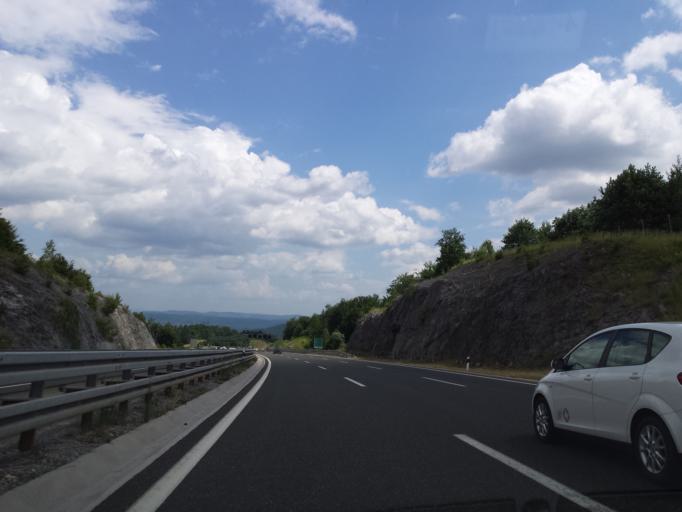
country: HR
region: Primorsko-Goranska
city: Vrbovsko
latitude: 45.3882
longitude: 15.1958
